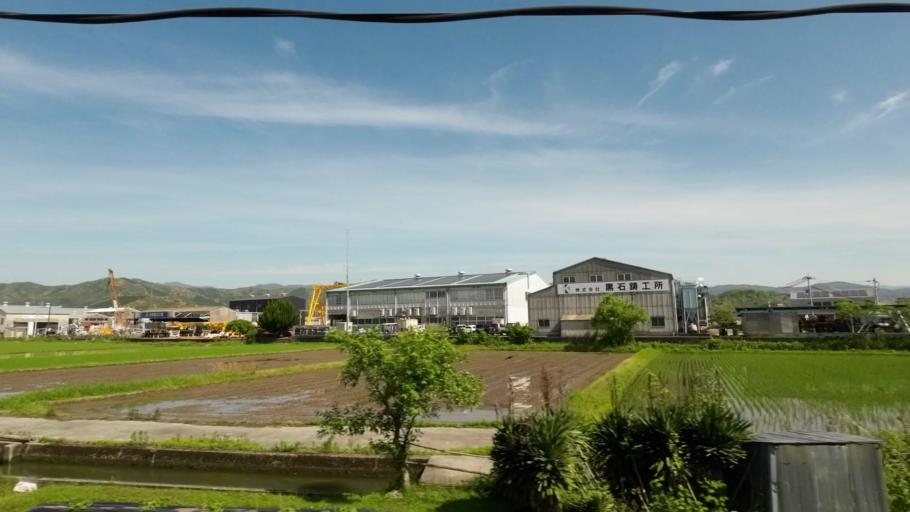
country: JP
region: Kochi
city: Kochi-shi
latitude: 33.5784
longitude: 133.6182
